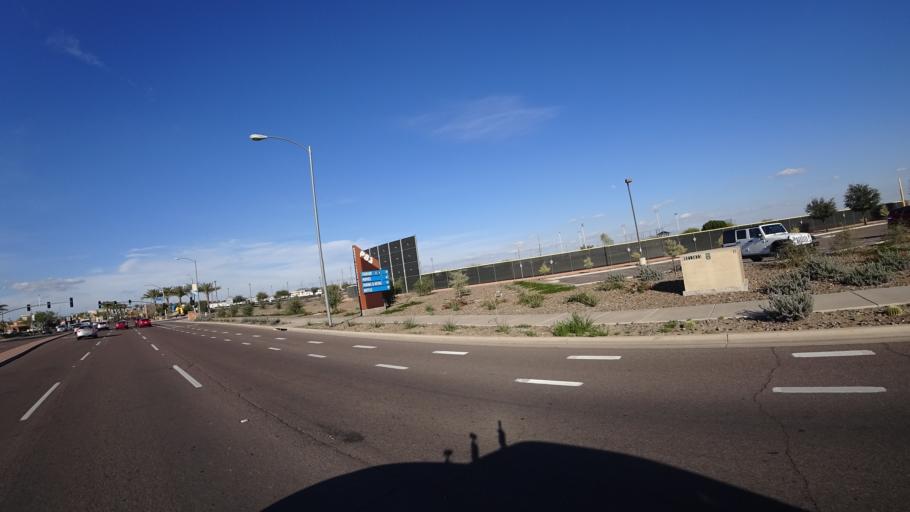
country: US
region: Arizona
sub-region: Maricopa County
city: Sun City
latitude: 33.6277
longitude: -112.2374
